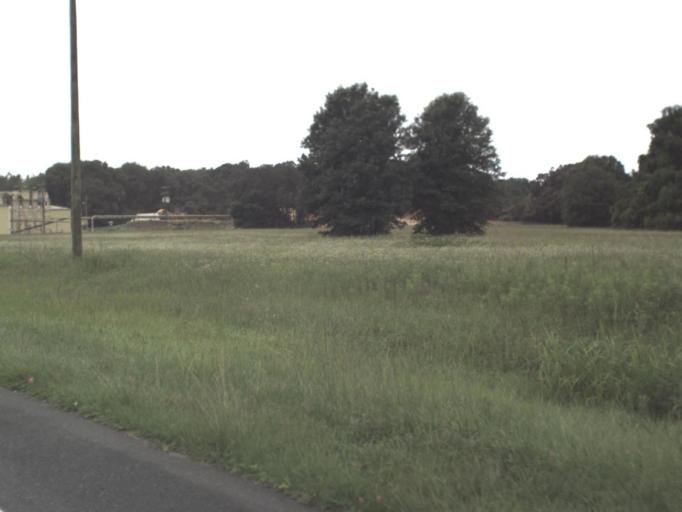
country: US
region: Florida
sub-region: Levy County
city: Williston
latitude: 29.3731
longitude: -82.4559
